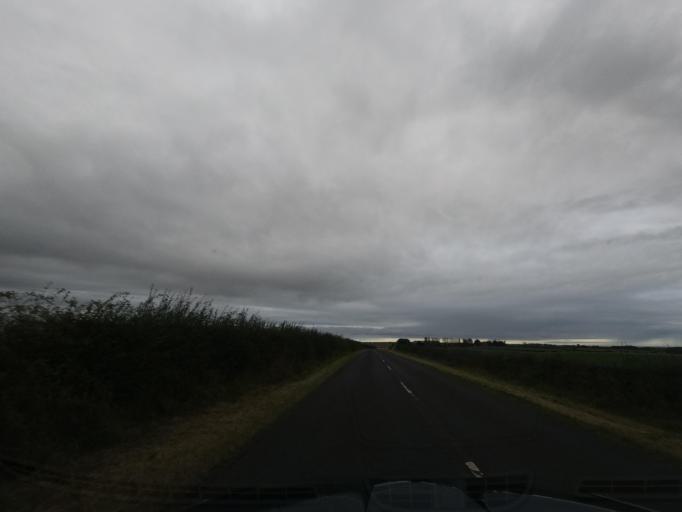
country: GB
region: England
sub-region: Northumberland
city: Ford
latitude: 55.6995
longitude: -2.0682
